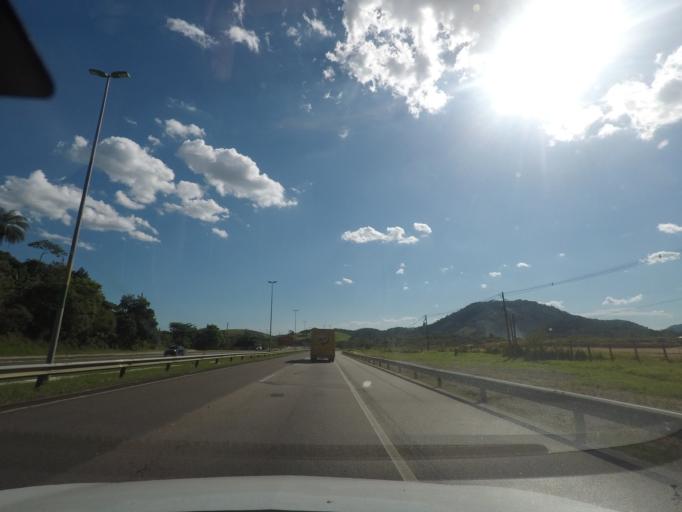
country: BR
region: Rio de Janeiro
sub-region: Guapimirim
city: Guapimirim
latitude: -22.5839
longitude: -43.0153
